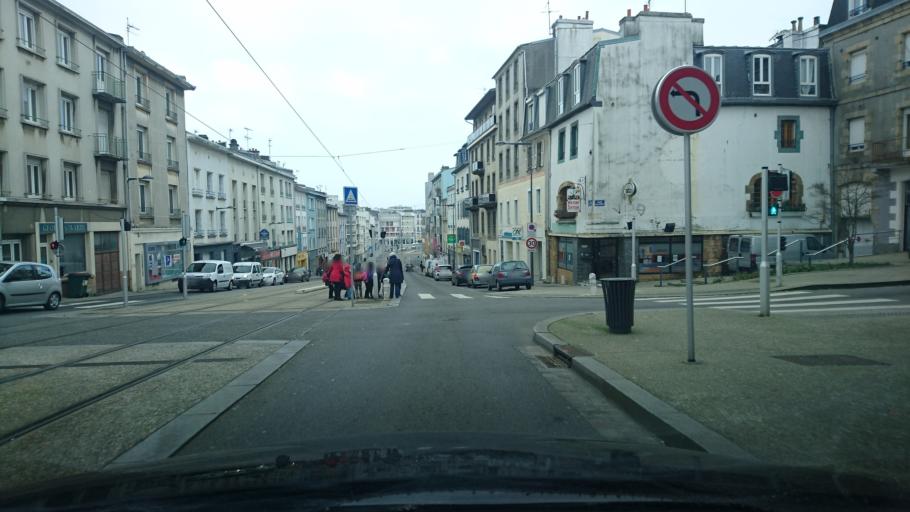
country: FR
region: Brittany
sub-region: Departement du Finistere
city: Brest
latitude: 48.3841
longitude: -4.5026
